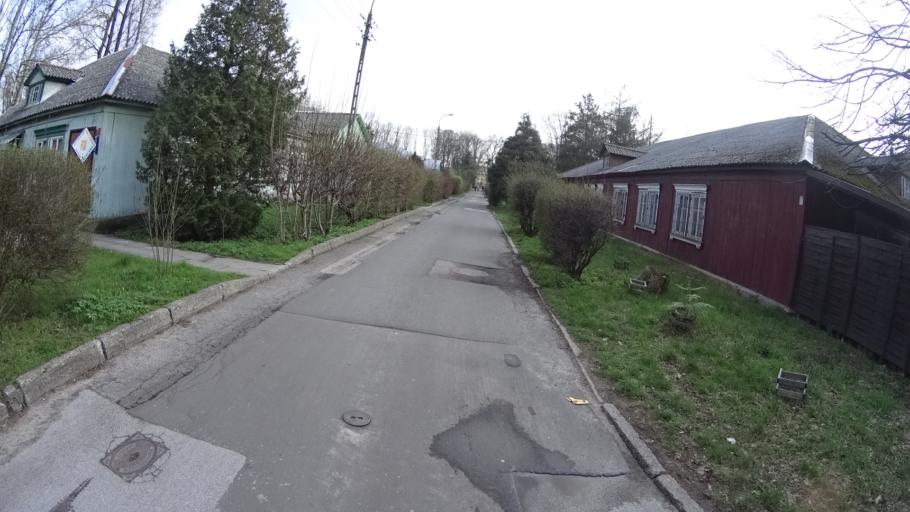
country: PL
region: Masovian Voivodeship
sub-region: Warszawa
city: Bemowo
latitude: 52.2377
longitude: 20.9195
